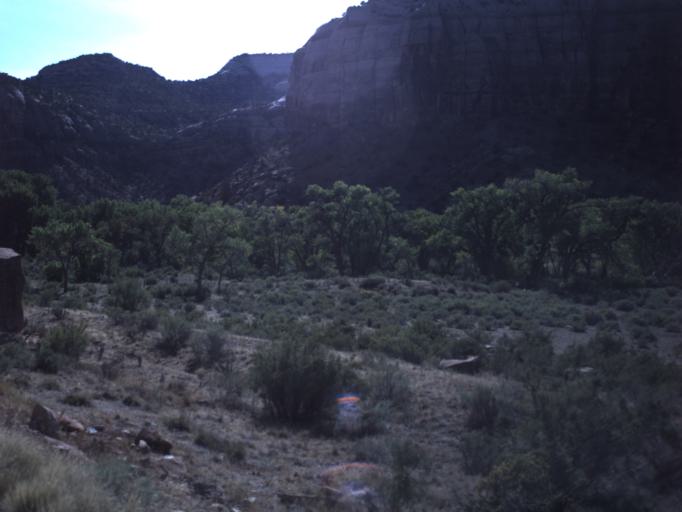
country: US
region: Utah
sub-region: San Juan County
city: Monticello
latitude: 38.0412
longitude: -109.5530
